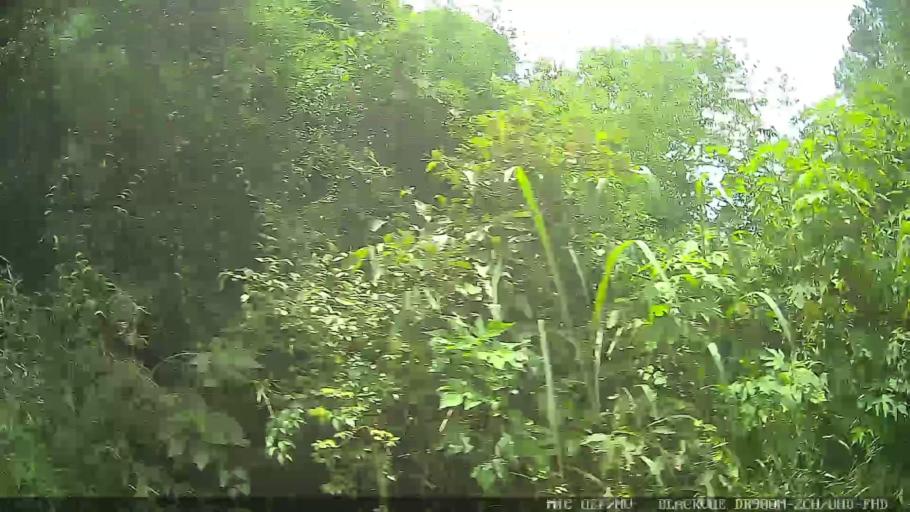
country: BR
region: Sao Paulo
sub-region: Santa Isabel
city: Santa Isabel
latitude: -23.3789
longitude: -46.2329
